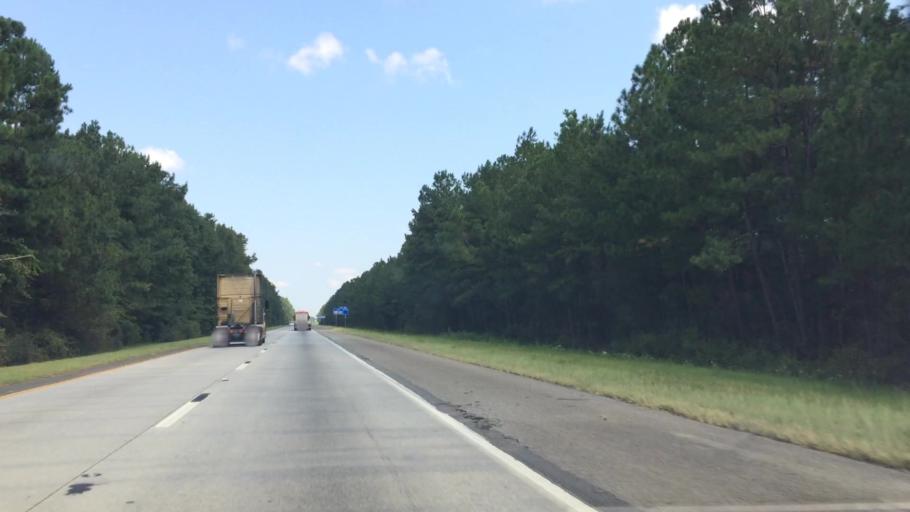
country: US
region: South Carolina
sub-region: Dorchester County
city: Saint George
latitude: 33.0691
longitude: -80.6595
